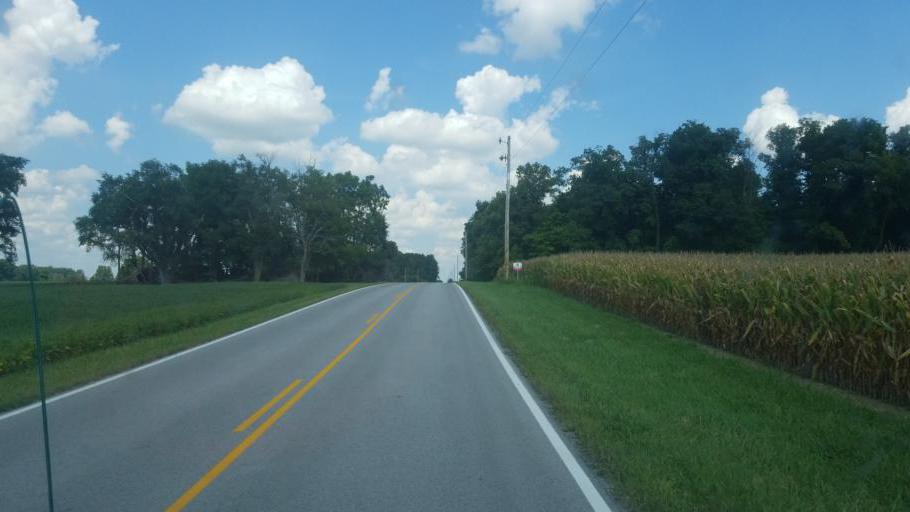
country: US
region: Ohio
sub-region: Hancock County
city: Arlington
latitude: 40.8493
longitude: -83.7276
